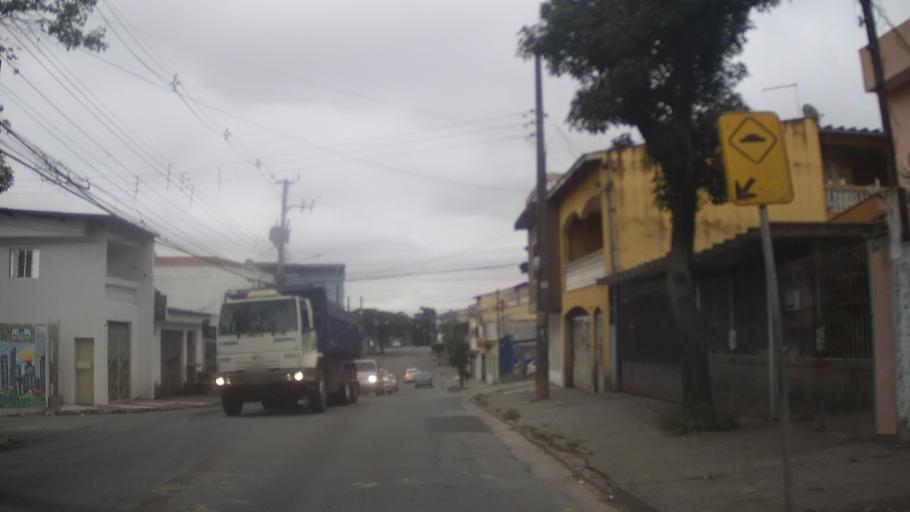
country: BR
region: Sao Paulo
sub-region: Guarulhos
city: Guarulhos
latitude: -23.4337
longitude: -46.5143
